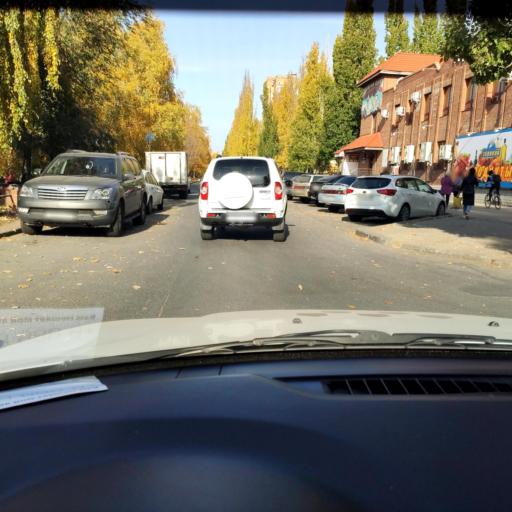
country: RU
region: Samara
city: Tol'yatti
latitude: 53.5302
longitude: 49.2983
